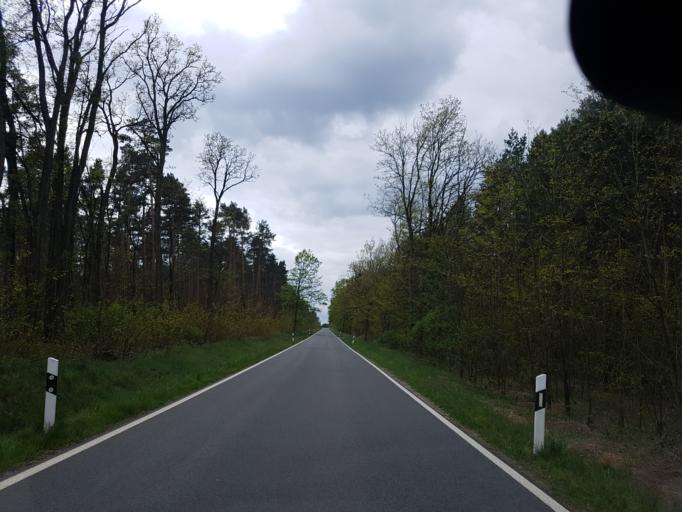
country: DE
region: Brandenburg
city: Altdobern
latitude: 51.6514
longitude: 13.9885
